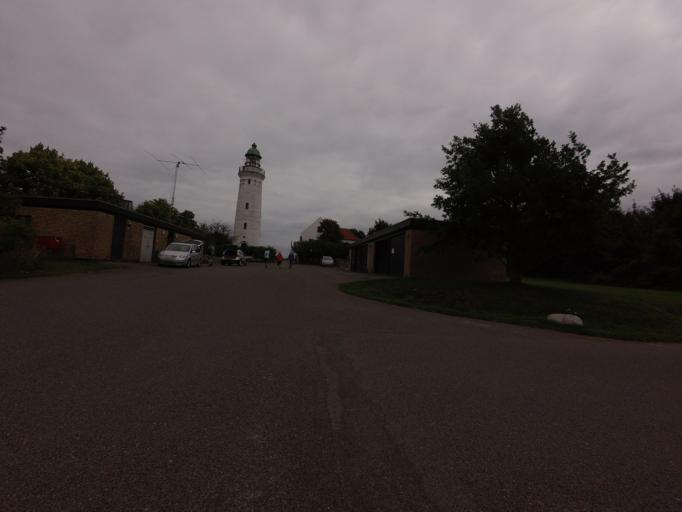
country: DK
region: Zealand
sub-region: Stevns Kommune
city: Store Heddinge
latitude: 55.2907
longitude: 12.4525
